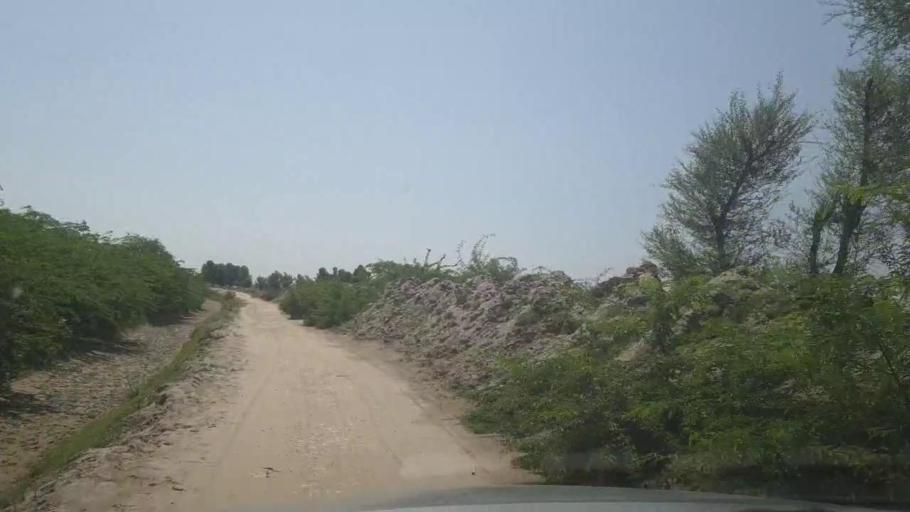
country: PK
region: Sindh
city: Khairpur
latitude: 27.3524
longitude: 69.0451
